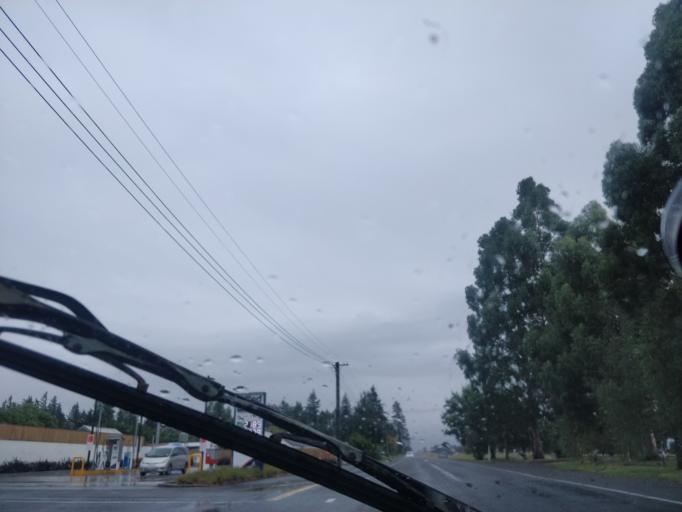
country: NZ
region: Canterbury
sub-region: Selwyn District
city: Darfield
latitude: -43.3875
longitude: 172.0170
